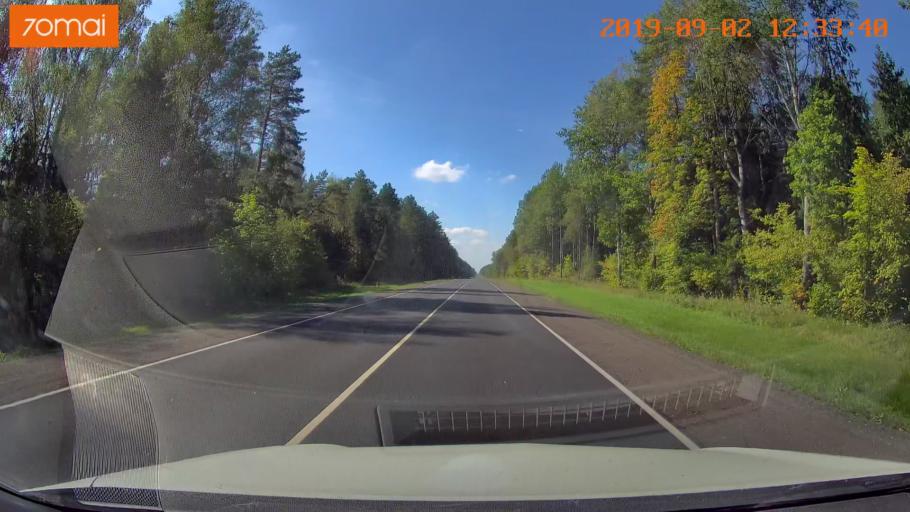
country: RU
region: Smolensk
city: Shumyachi
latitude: 53.8161
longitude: 32.4230
